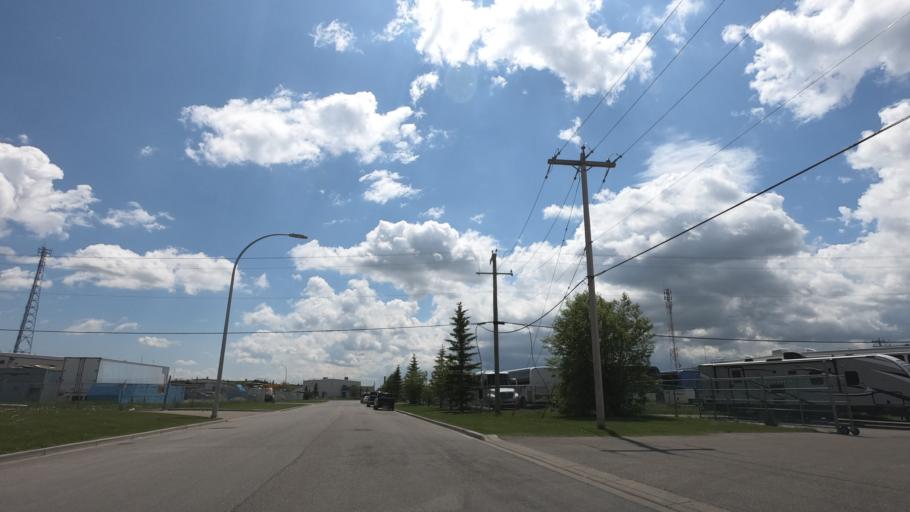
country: CA
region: Alberta
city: Airdrie
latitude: 51.2947
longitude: -113.9950
